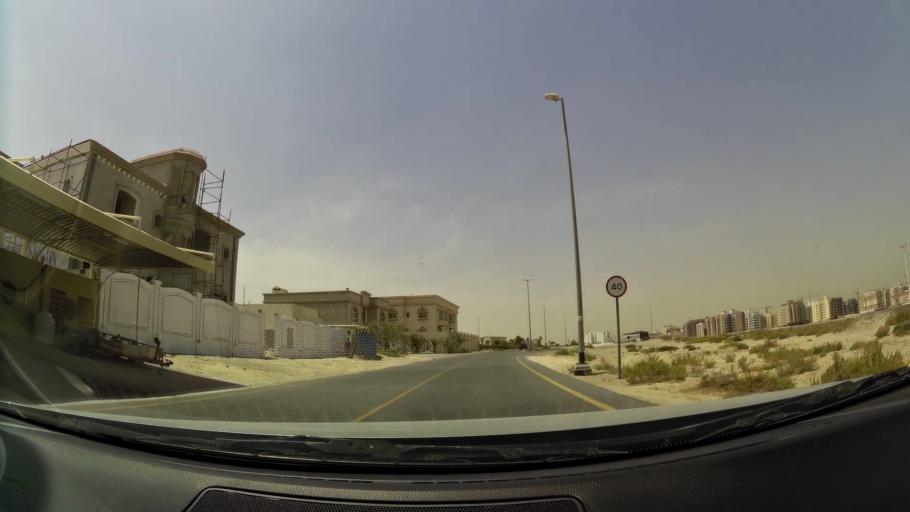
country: AE
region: Ash Shariqah
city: Sharjah
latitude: 25.1910
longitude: 55.4127
